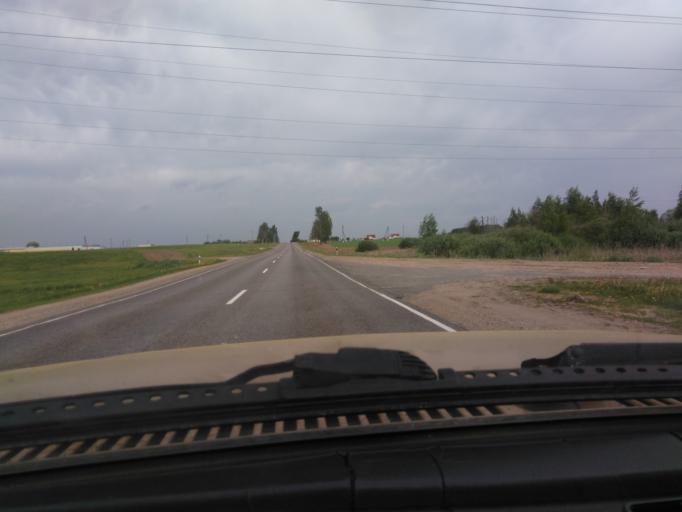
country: BY
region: Mogilev
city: Palykavichy Pyershyya
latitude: 54.0176
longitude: 30.3218
